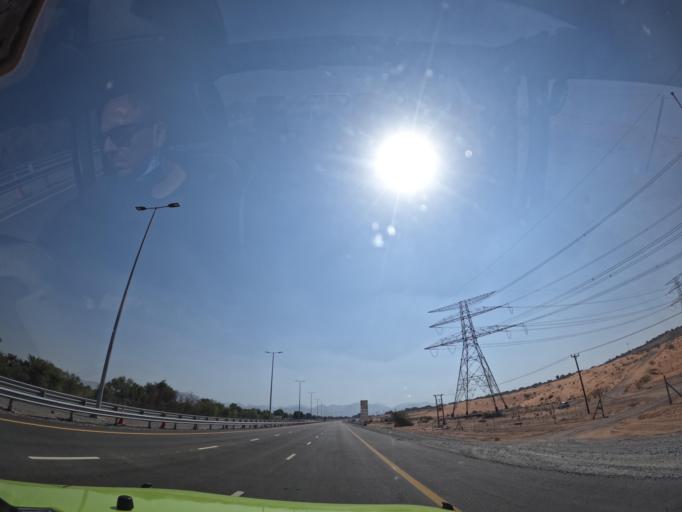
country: AE
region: Ash Shariqah
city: Adh Dhayd
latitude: 24.7921
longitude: 55.8101
